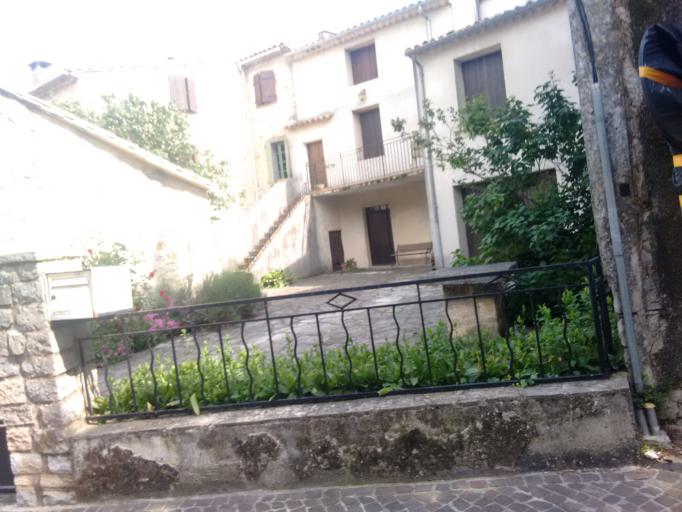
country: FR
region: Languedoc-Roussillon
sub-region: Departement de l'Herault
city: Saint-Martin-de-Londres
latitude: 43.7904
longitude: 3.7314
